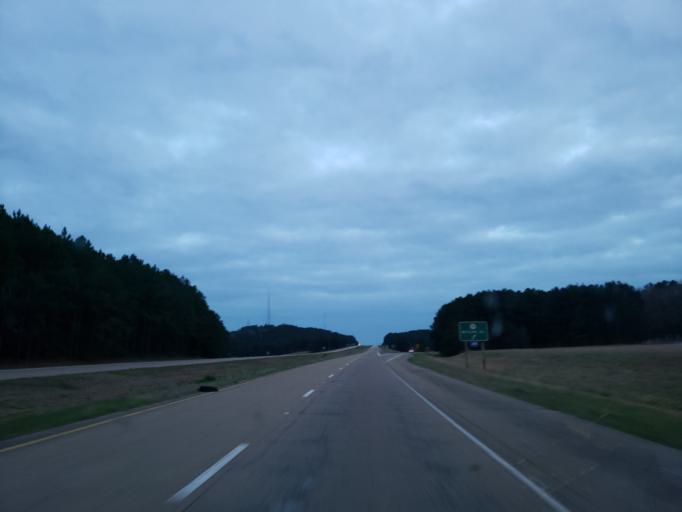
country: US
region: Mississippi
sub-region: Lauderdale County
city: Marion
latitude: 32.3730
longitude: -88.6352
